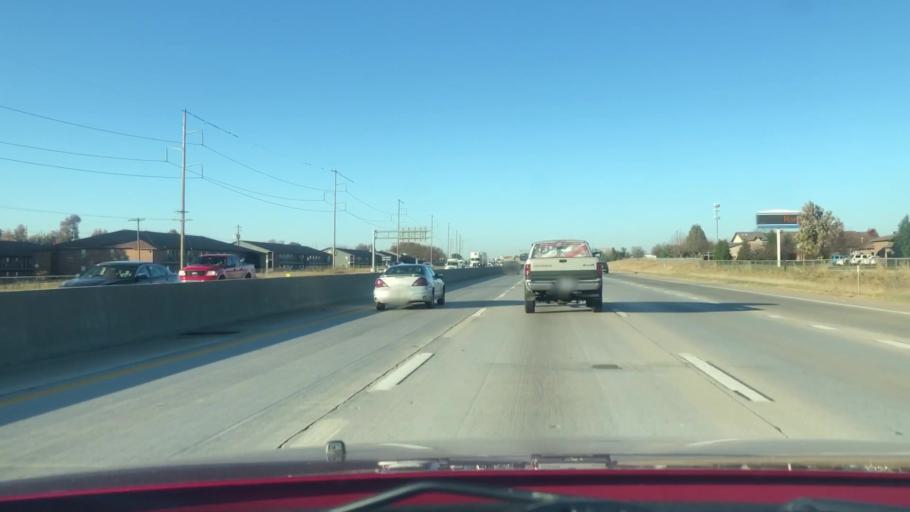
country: US
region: Missouri
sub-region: Greene County
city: Springfield
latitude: 37.1721
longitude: -93.2242
